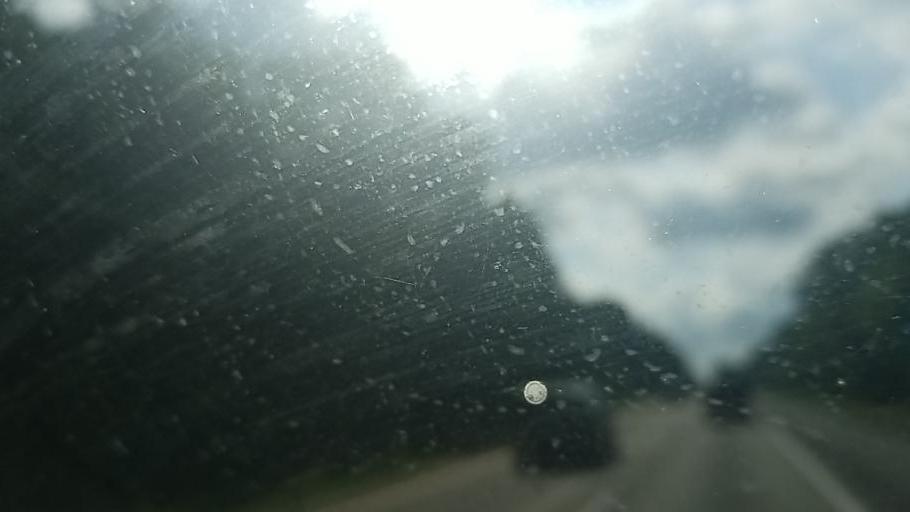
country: US
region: Pennsylvania
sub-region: Clearfield County
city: Troy
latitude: 40.9934
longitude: -78.2130
